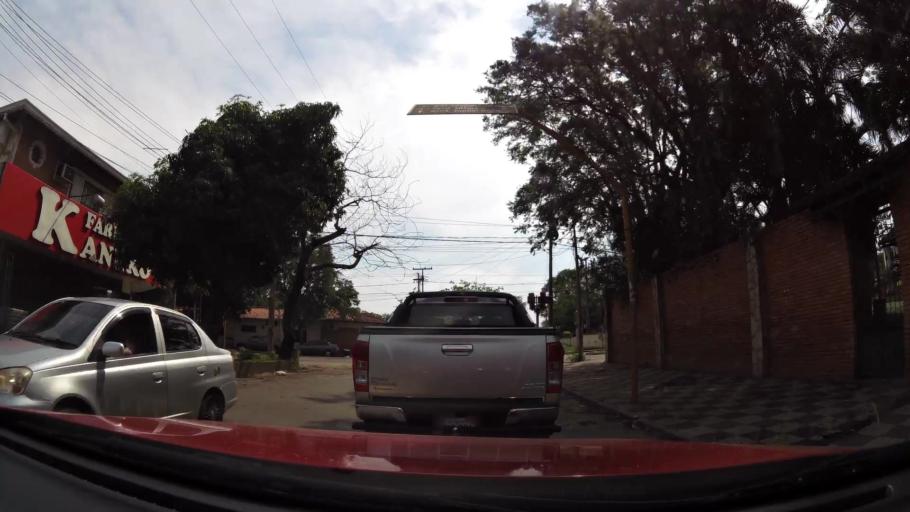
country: PY
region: Asuncion
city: Asuncion
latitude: -25.2610
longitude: -57.5772
